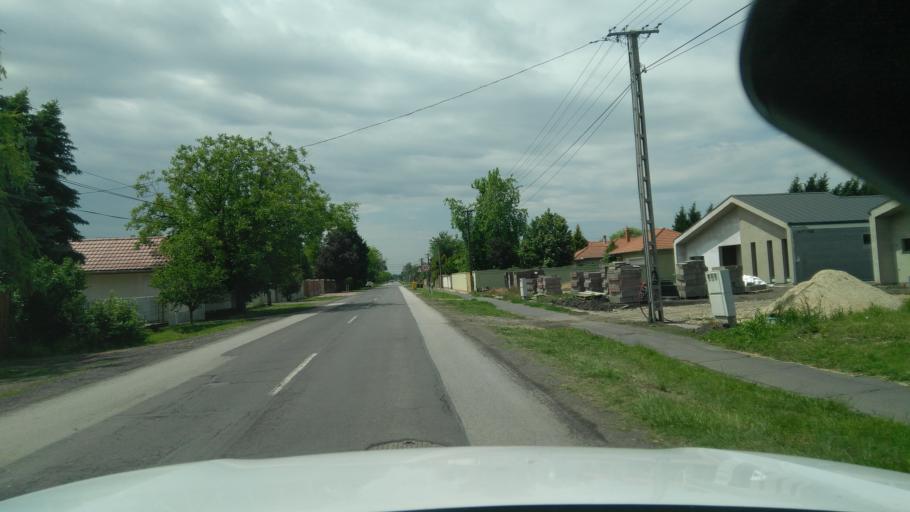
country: HU
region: Bekes
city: Bekescsaba
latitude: 46.6959
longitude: 21.1341
